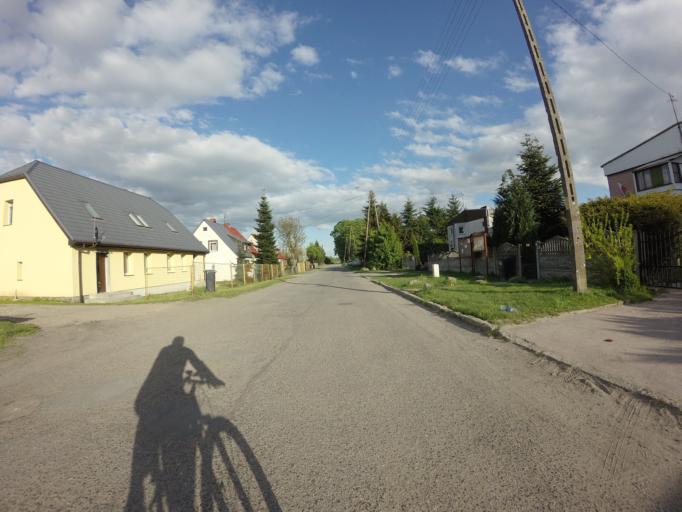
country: PL
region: West Pomeranian Voivodeship
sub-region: Powiat choszczenski
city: Choszczno
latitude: 53.1570
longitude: 15.3938
